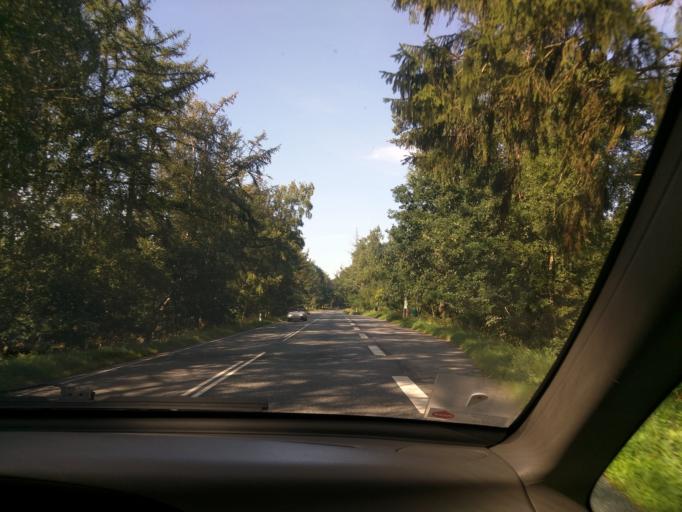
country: DK
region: Central Jutland
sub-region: Viborg Kommune
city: Bjerringbro
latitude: 56.3041
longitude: 9.6855
